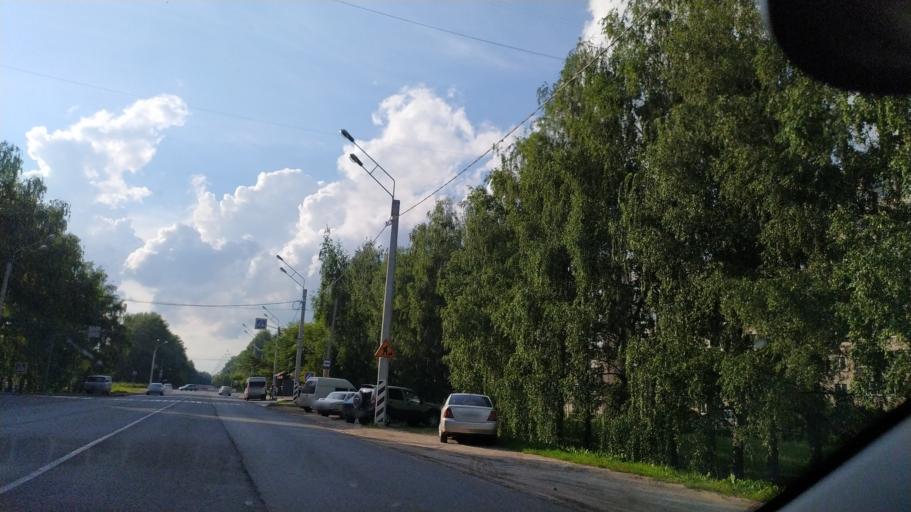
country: RU
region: Chuvashia
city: Novocheboksarsk
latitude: 56.1126
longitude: 47.4419
